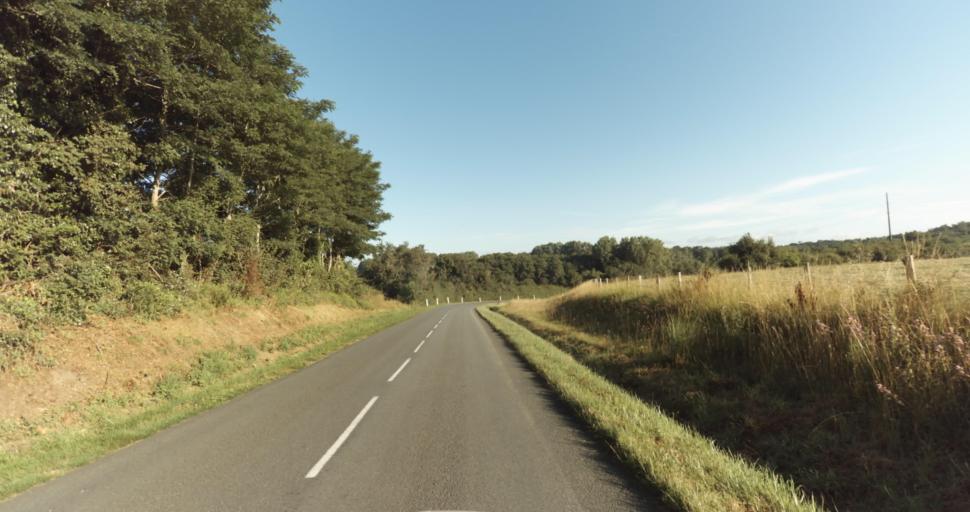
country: FR
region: Aquitaine
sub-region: Departement de la Gironde
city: Bazas
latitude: 44.4022
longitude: -0.2051
